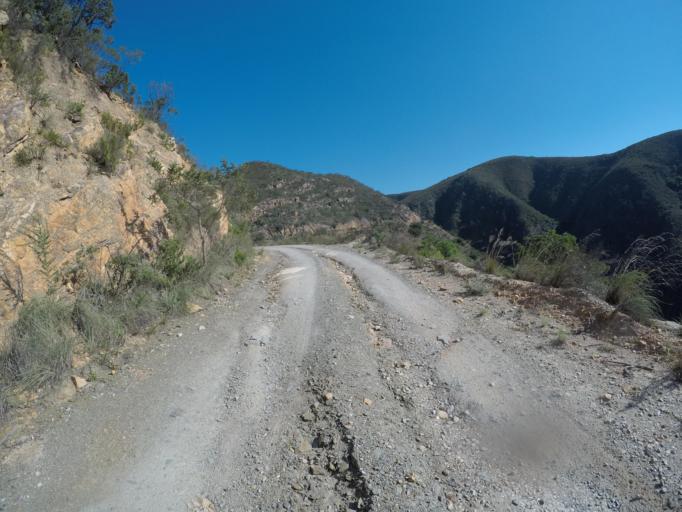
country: ZA
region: Eastern Cape
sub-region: Cacadu District Municipality
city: Kareedouw
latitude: -33.6536
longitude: 24.5074
